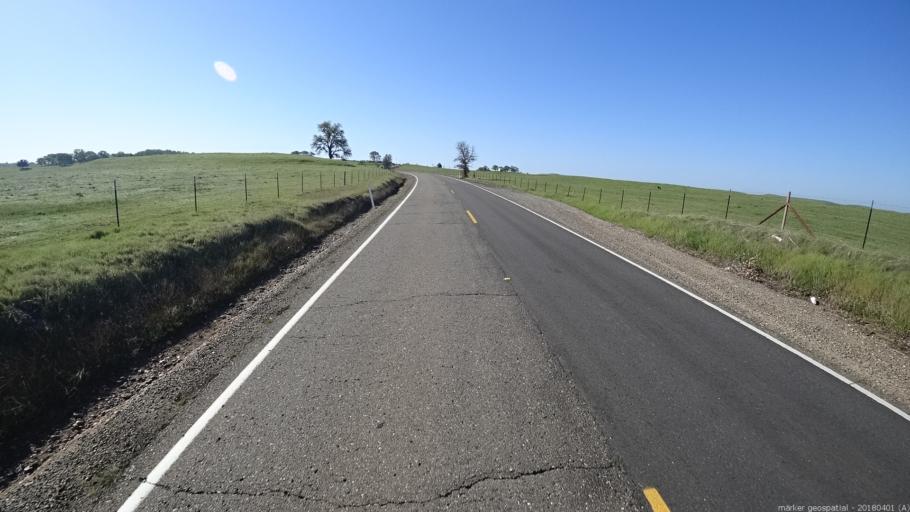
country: US
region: California
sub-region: Sacramento County
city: Rancho Murieta
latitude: 38.4691
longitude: -121.0441
